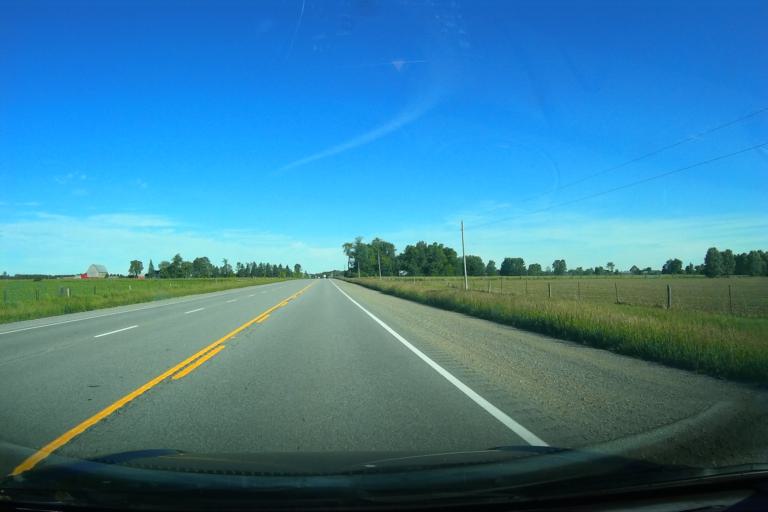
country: CA
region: Ontario
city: Pembroke
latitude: 45.6562
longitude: -76.9125
